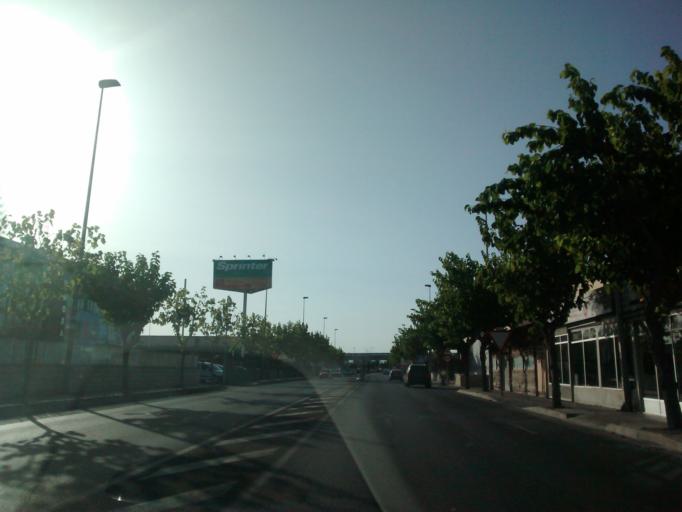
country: ES
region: Valencia
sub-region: Provincia de Alicante
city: Santa Pola
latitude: 38.1987
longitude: -0.5661
